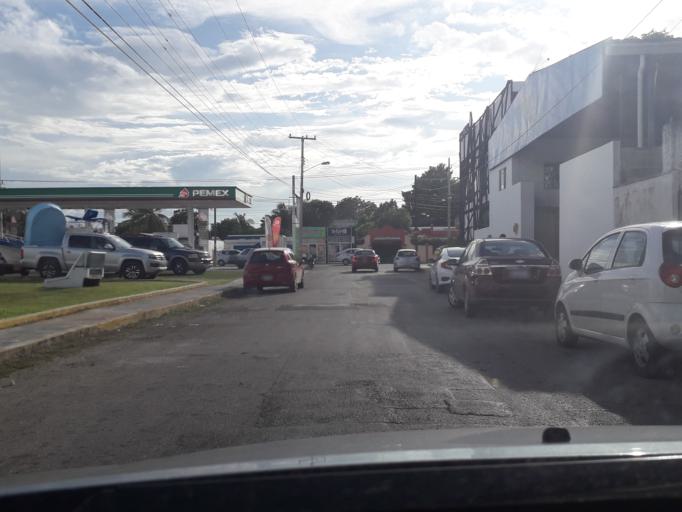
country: MX
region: Yucatan
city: Merida
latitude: 21.0025
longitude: -89.6385
